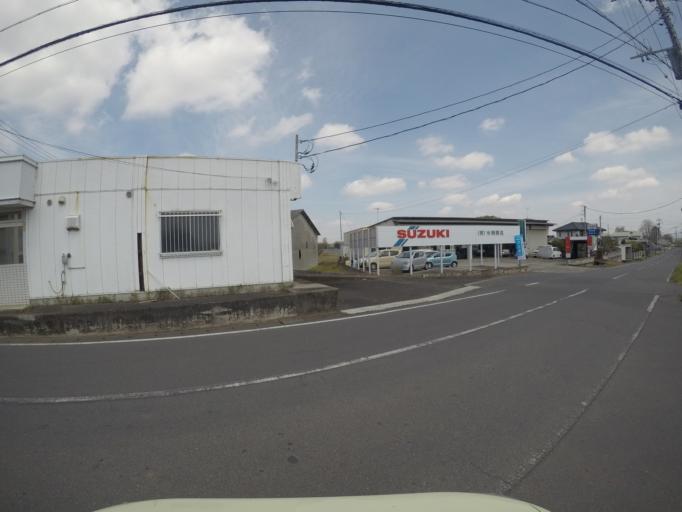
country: JP
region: Ibaraki
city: Shimodate
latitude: 36.2703
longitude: 140.0156
